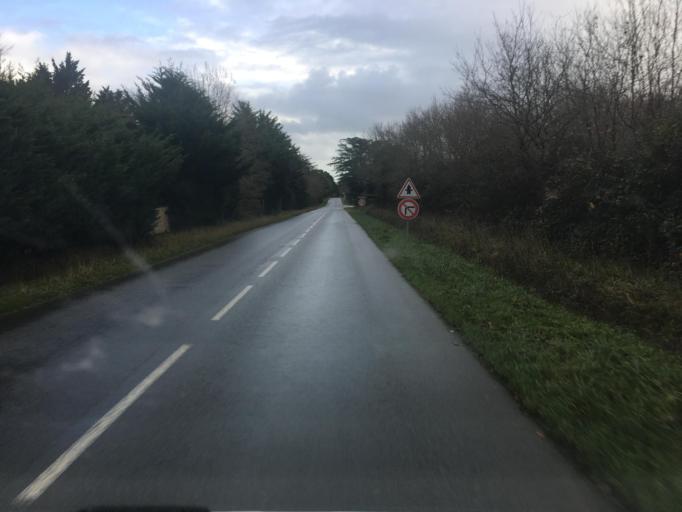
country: FR
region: Brittany
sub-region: Departement du Morbihan
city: Surzur
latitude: 47.5191
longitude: -2.6760
